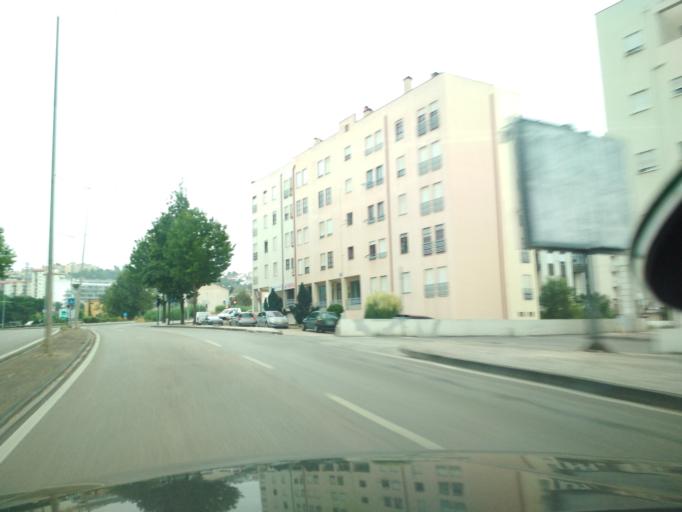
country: PT
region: Coimbra
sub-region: Coimbra
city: Coimbra
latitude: 40.1936
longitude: -8.4039
